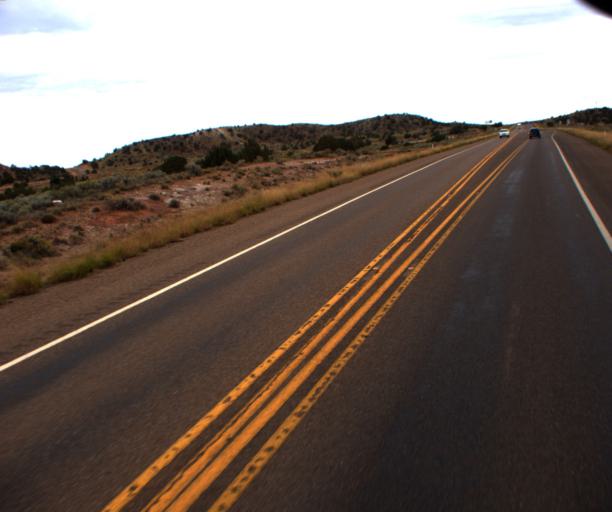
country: US
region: Arizona
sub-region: Navajo County
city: Taylor
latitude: 34.4502
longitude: -110.0926
